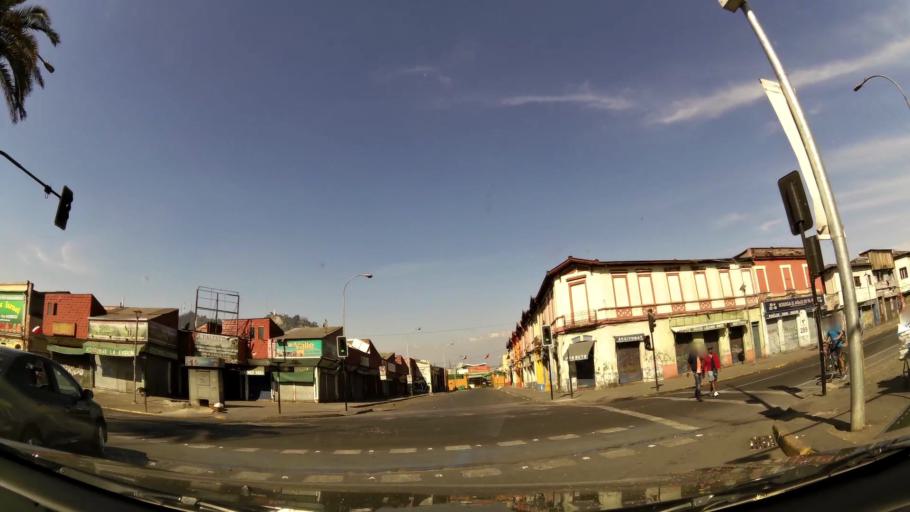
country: CL
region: Santiago Metropolitan
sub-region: Provincia de Santiago
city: Santiago
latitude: -33.4286
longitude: -70.6516
